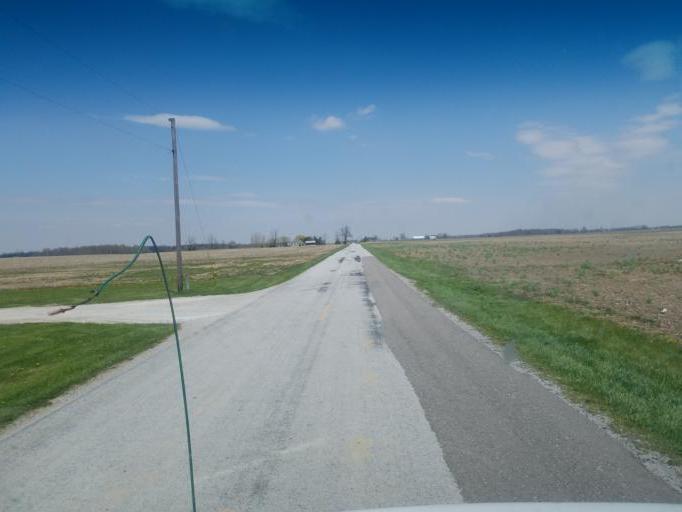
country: US
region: Ohio
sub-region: Hardin County
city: Kenton
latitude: 40.7066
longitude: -83.5379
